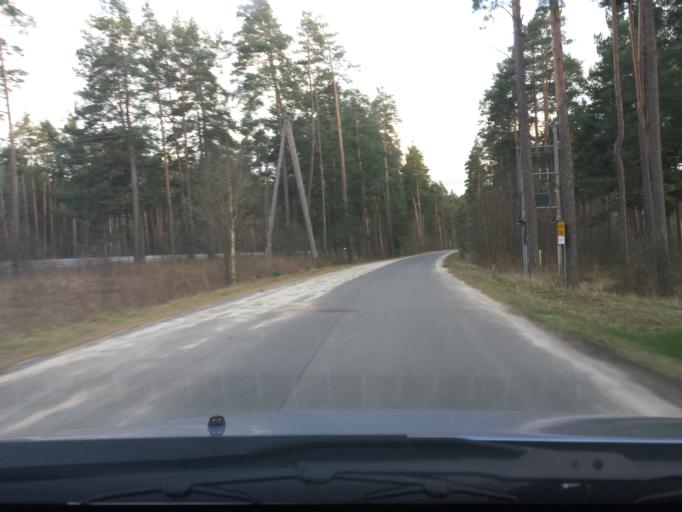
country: LV
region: Adazi
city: Adazi
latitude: 57.0300
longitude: 24.3202
